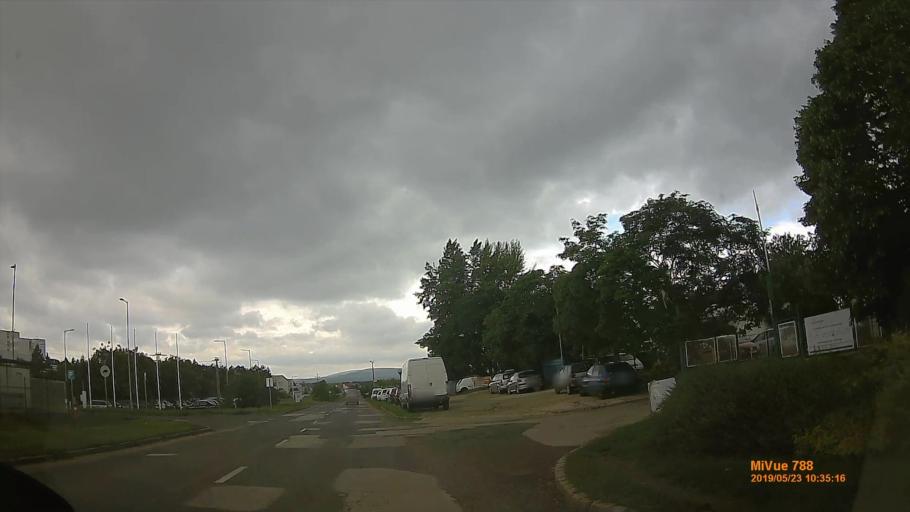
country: HU
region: Veszprem
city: Veszprem
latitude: 47.1083
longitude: 17.8922
